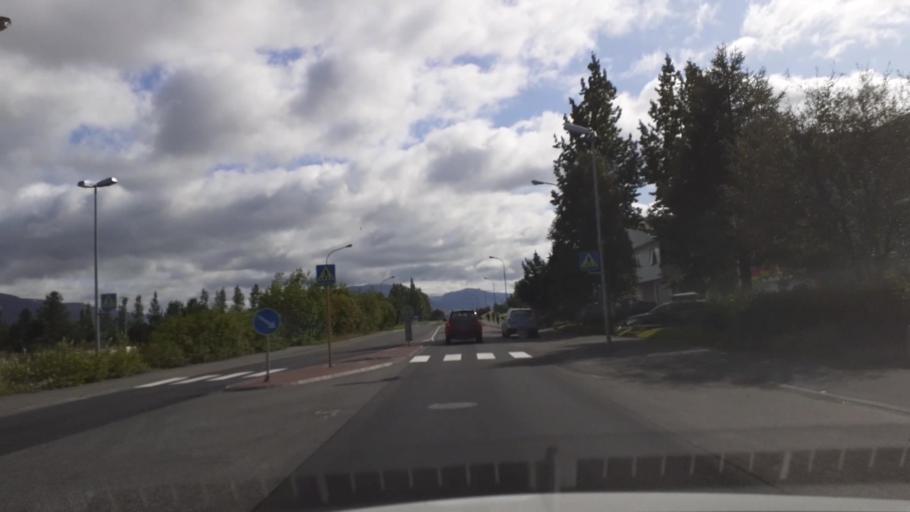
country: IS
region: Northeast
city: Akureyri
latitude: 65.6759
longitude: -18.0980
